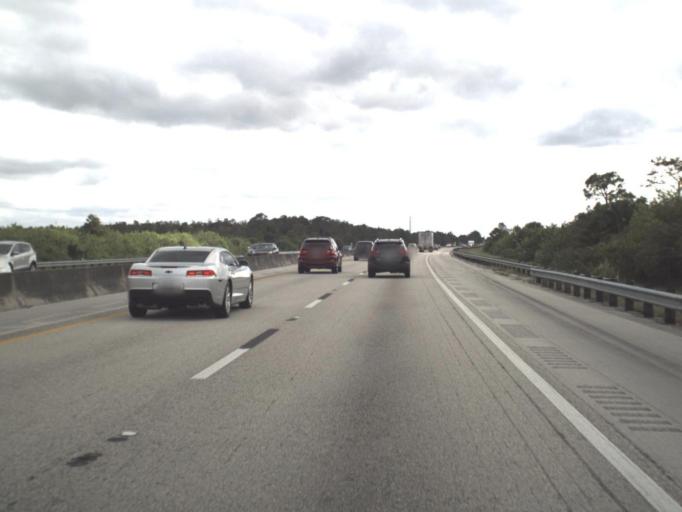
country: US
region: Florida
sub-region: Martin County
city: Port Salerno
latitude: 27.0548
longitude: -80.2401
